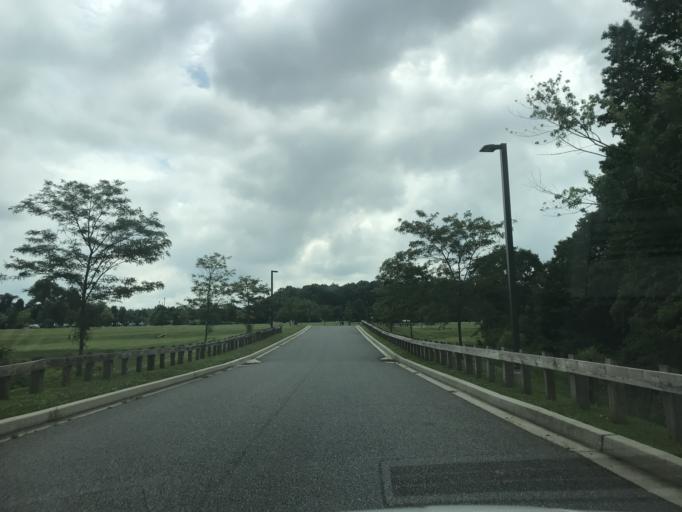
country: US
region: Maryland
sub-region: Harford County
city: South Bel Air
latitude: 39.5491
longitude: -76.2842
